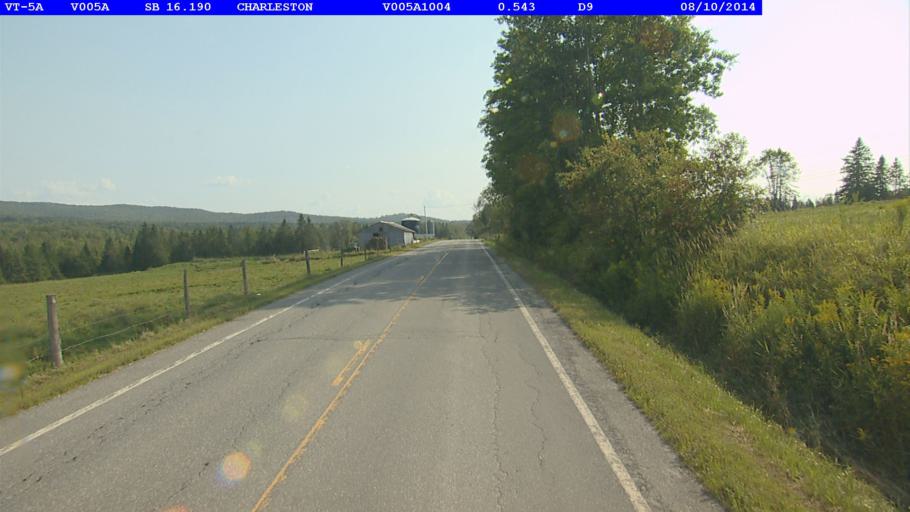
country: US
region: Vermont
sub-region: Orleans County
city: Newport
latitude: 44.8419
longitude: -72.0609
